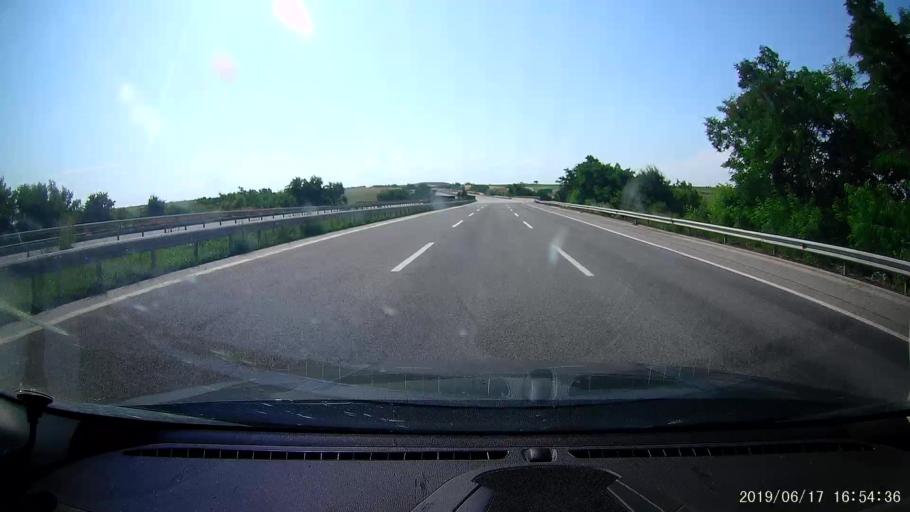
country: TR
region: Kirklareli
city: Inece
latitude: 41.5748
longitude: 26.9911
